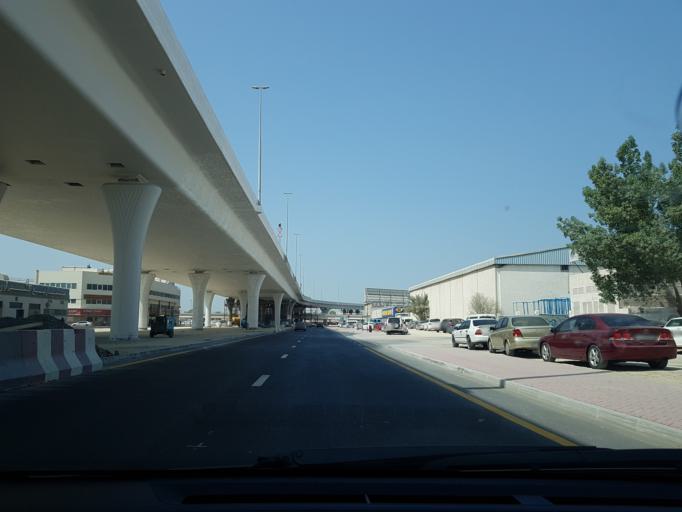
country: AE
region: Dubai
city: Dubai
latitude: 25.1576
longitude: 55.2328
